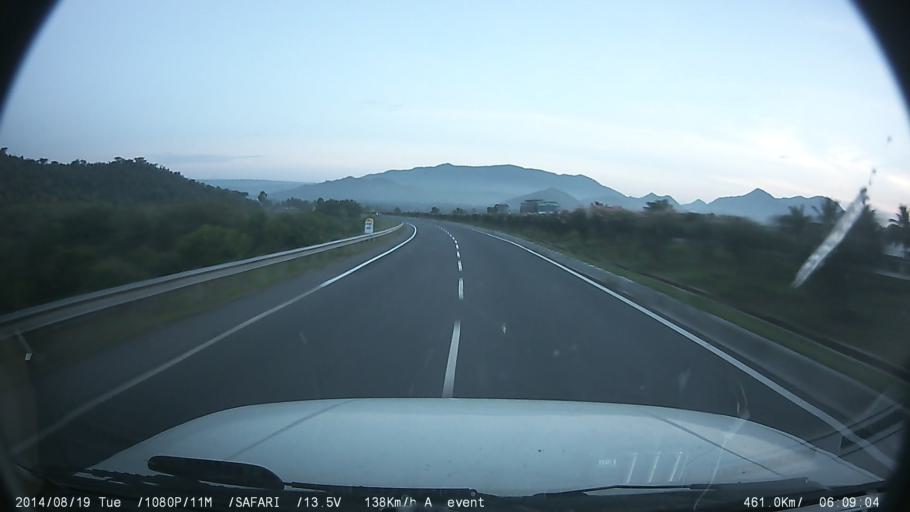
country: IN
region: Tamil Nadu
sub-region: Salem
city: Omalur
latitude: 11.9295
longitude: 78.0650
